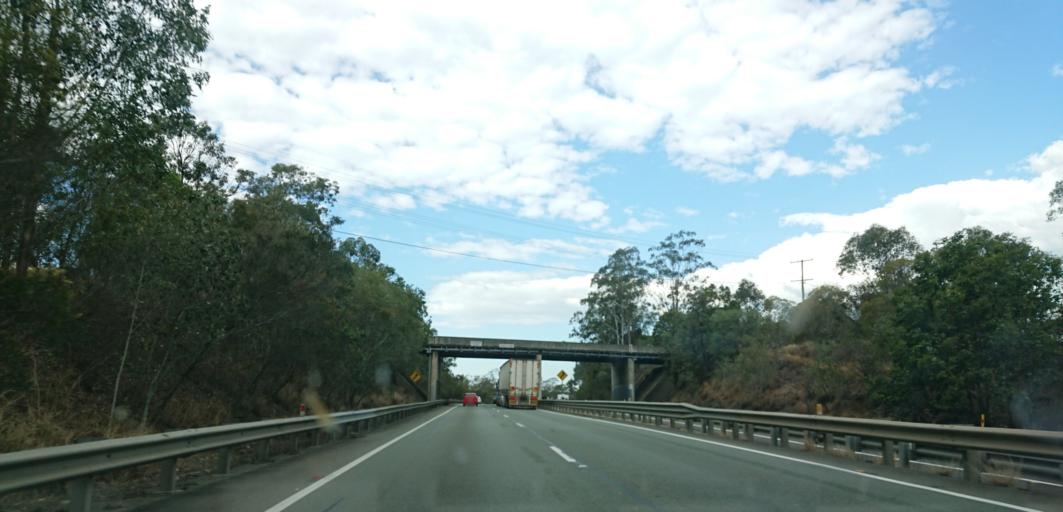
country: AU
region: Queensland
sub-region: Ipswich
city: Brassall
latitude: -27.5805
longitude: 152.7521
